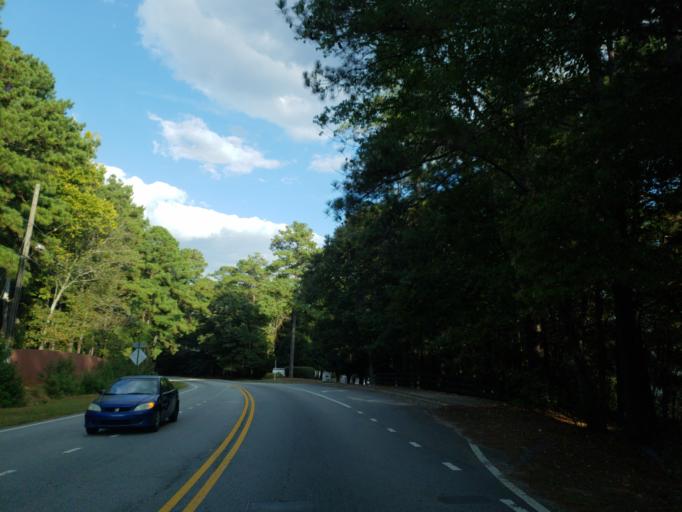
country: US
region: Georgia
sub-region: Cobb County
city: Mableton
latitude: 33.7509
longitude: -84.5800
